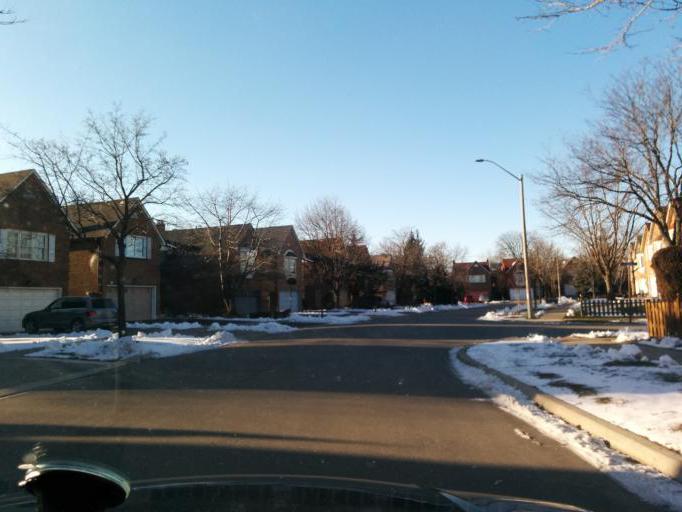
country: CA
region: Ontario
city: Mississauga
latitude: 43.5715
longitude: -79.6627
